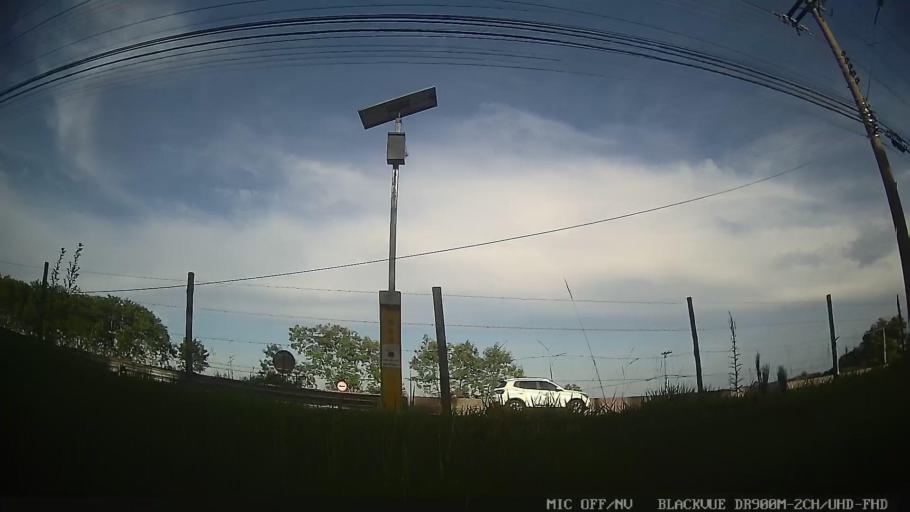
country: BR
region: Sao Paulo
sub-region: Tiete
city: Tiete
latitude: -23.0688
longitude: -47.7294
